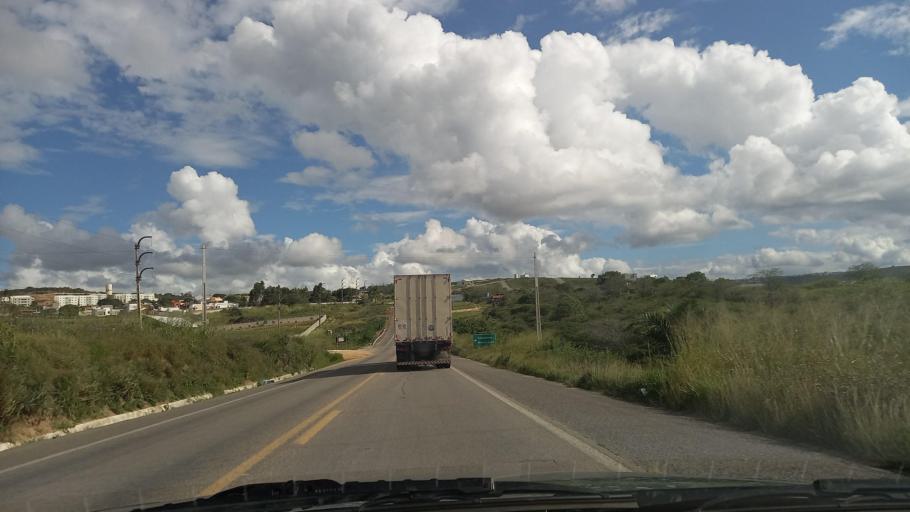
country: BR
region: Pernambuco
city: Garanhuns
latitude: -8.8510
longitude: -36.4617
